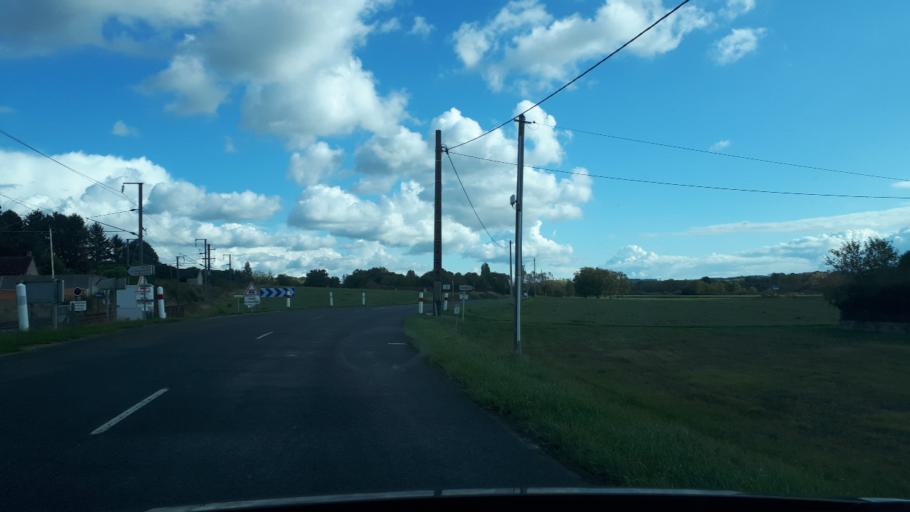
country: FR
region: Centre
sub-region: Departement du Loir-et-Cher
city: Mareuil-sur-Cher
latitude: 47.3129
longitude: 1.3347
